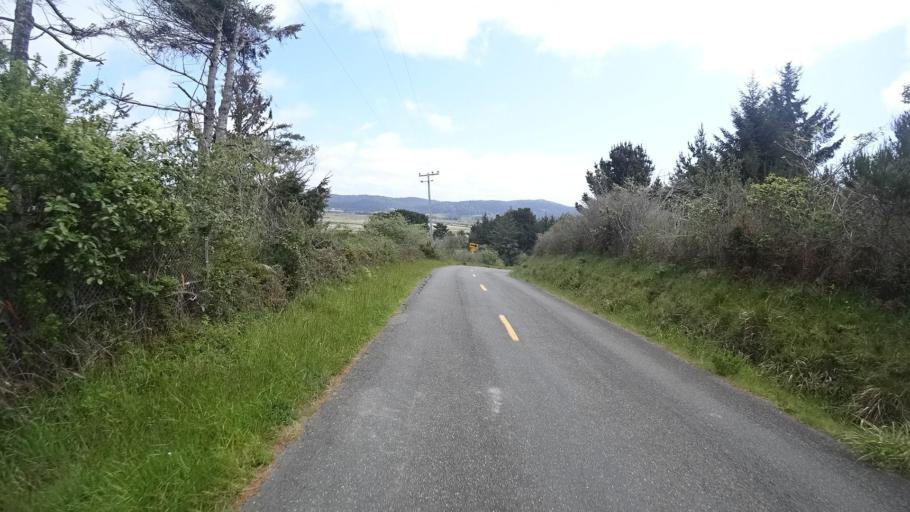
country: US
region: California
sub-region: Humboldt County
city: Humboldt Hill
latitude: 40.6867
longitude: -124.2367
